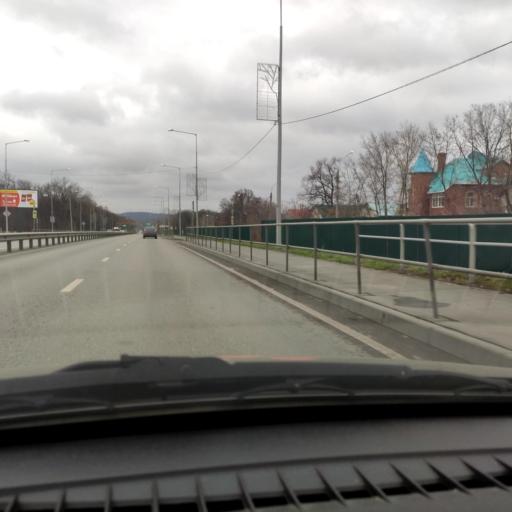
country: RU
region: Samara
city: Volzhskiy
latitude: 53.3538
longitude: 50.2114
